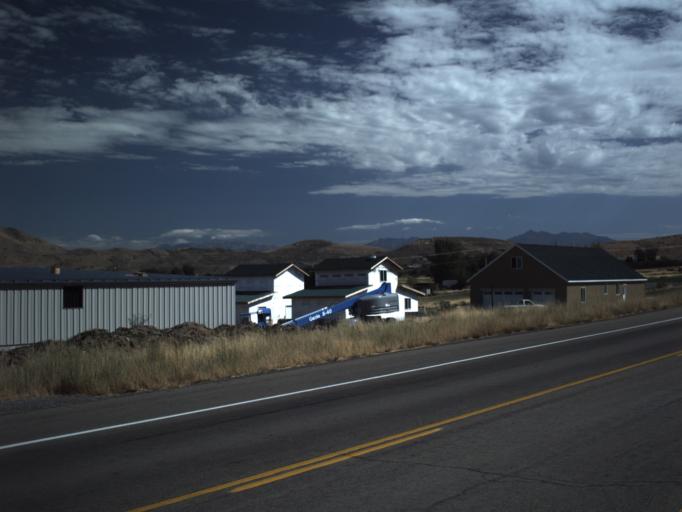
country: US
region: Utah
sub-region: Utah County
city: Genola
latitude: 39.9803
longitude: -111.8334
